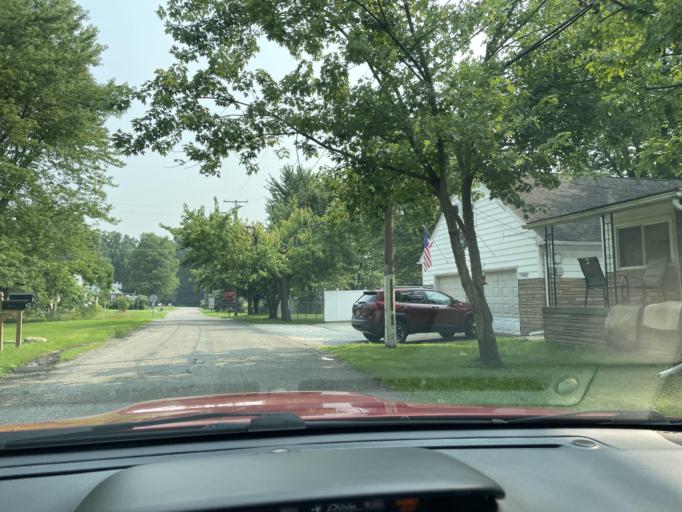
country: US
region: Ohio
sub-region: Trumbull County
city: McDonald
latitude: 41.1635
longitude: -80.7384
